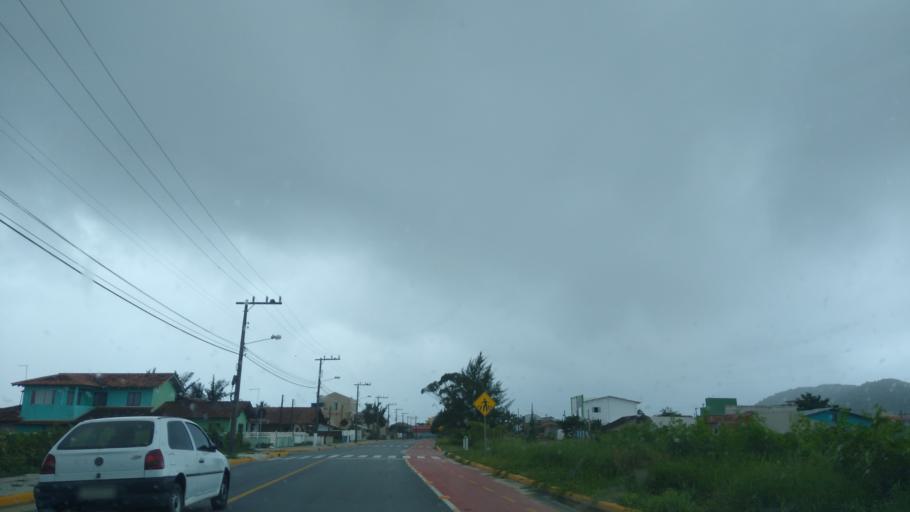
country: BR
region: Santa Catarina
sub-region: Sao Francisco Do Sul
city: Sao Francisco do Sul
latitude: -26.2353
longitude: -48.5113
